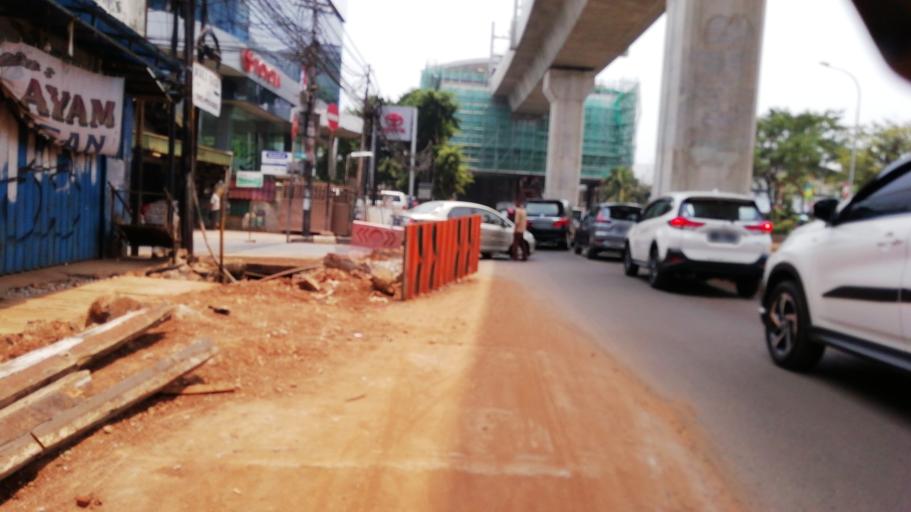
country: ID
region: Banten
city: South Tangerang
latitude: -6.2799
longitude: 106.7967
